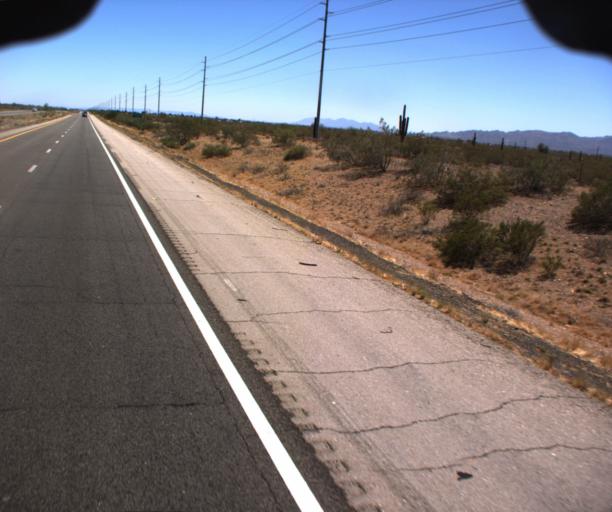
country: US
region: Arizona
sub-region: Maricopa County
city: Wickenburg
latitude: 33.8001
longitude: -112.5573
